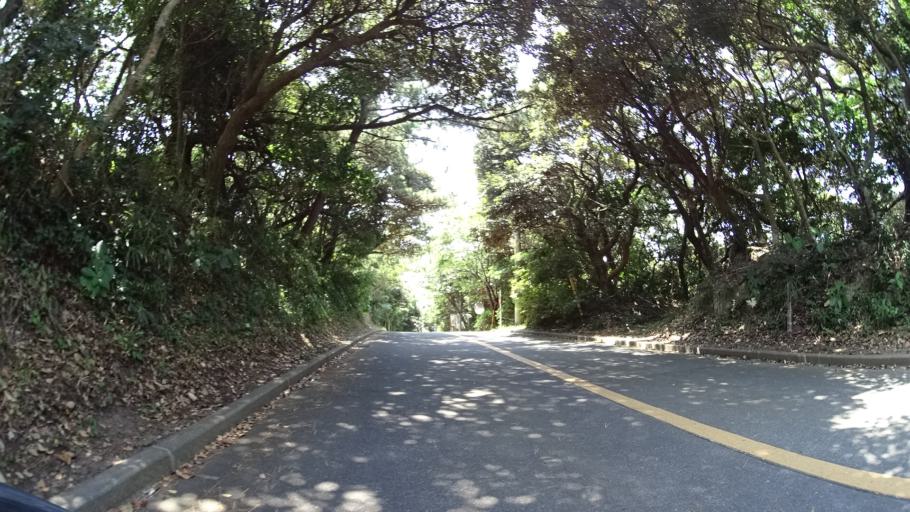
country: JP
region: Shizuoka
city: Shimoda
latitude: 34.3316
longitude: 139.2156
